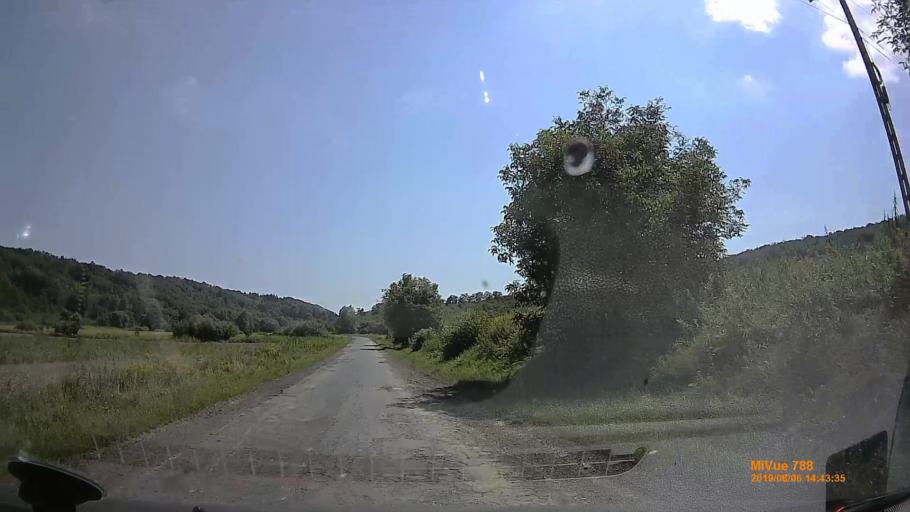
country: HU
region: Zala
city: Nagykanizsa
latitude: 46.5302
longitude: 17.0505
